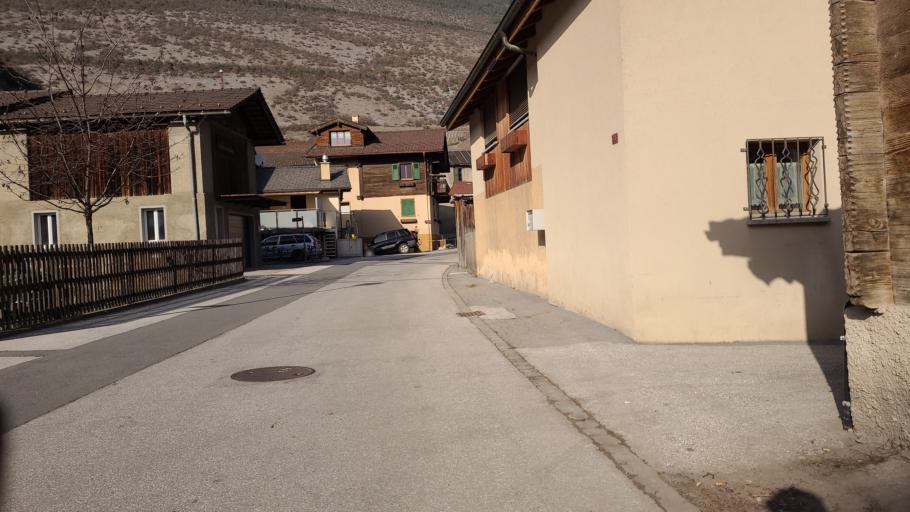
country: CH
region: Valais
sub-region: Leuk District
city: Salgesch
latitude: 46.3130
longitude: 7.5693
